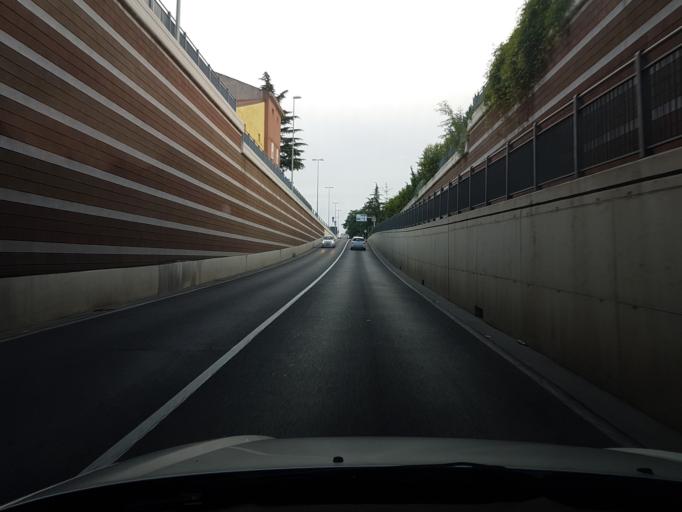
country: IT
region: Friuli Venezia Giulia
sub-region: Provincia di Gorizia
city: Ronchi dei Legionari
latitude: 45.8190
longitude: 13.5141
